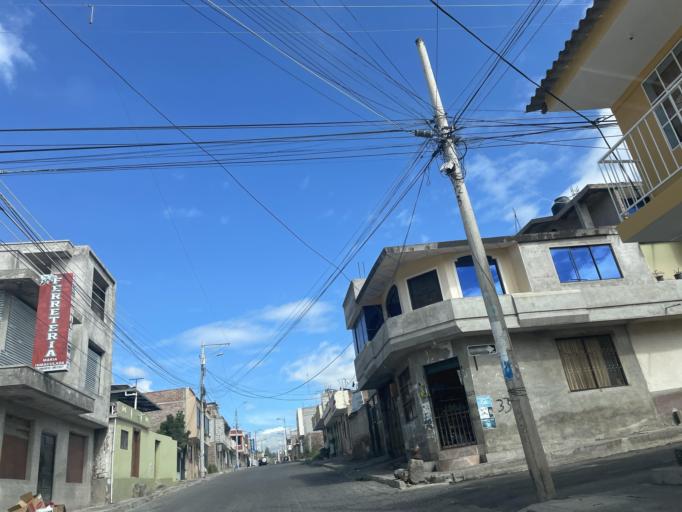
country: EC
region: Chimborazo
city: Guano
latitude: -1.6069
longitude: -78.6372
